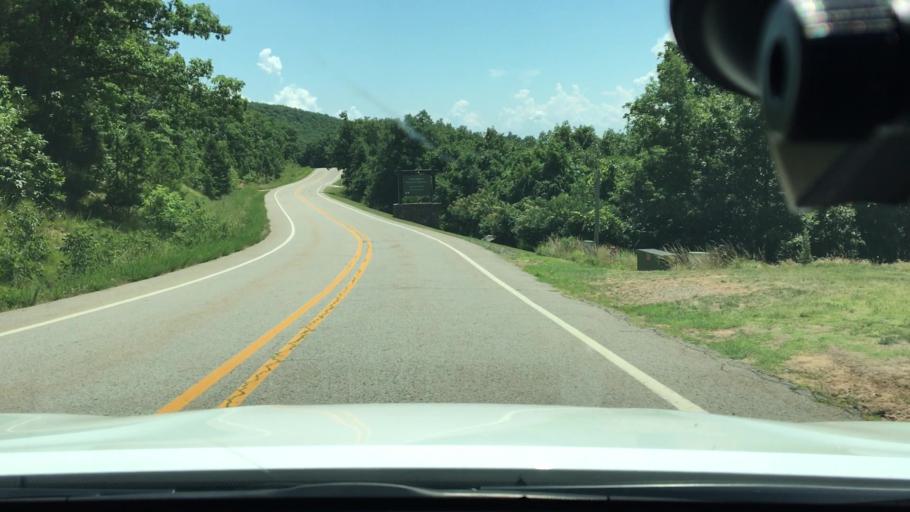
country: US
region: Arkansas
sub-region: Logan County
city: Paris
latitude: 35.1643
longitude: -93.6453
